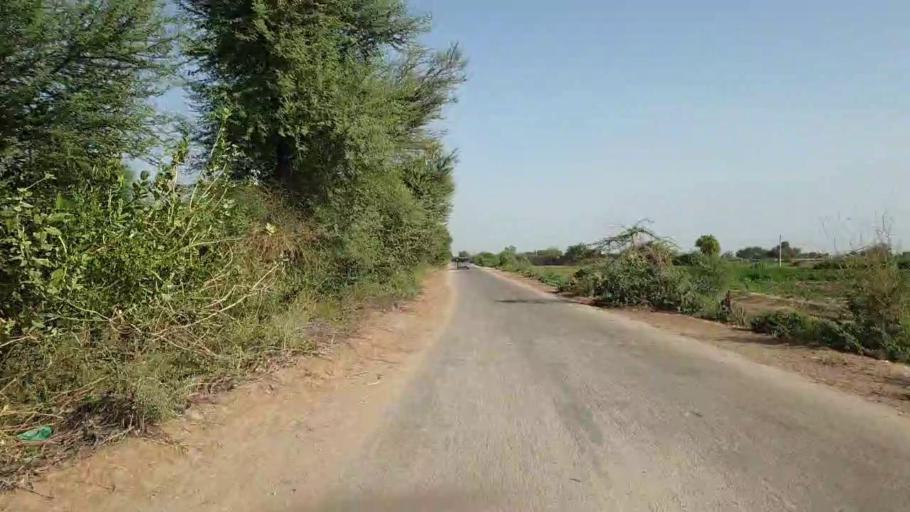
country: PK
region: Sindh
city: Nawabshah
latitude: 26.0927
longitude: 68.4711
